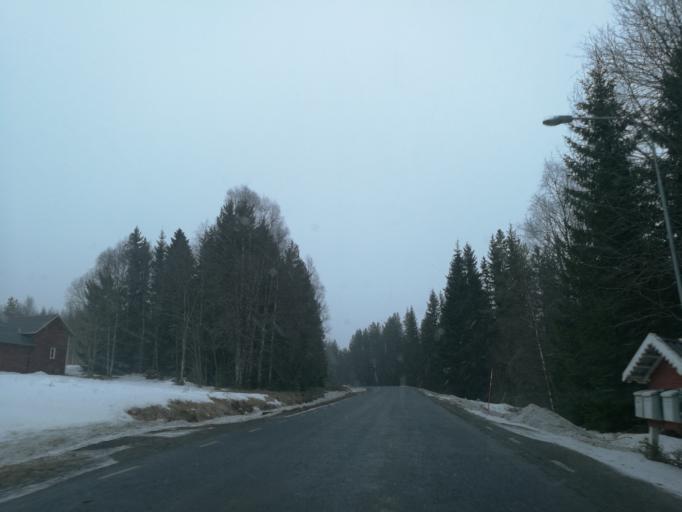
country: NO
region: Hedmark
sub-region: Grue
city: Kirkenaer
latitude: 60.7013
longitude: 12.6162
